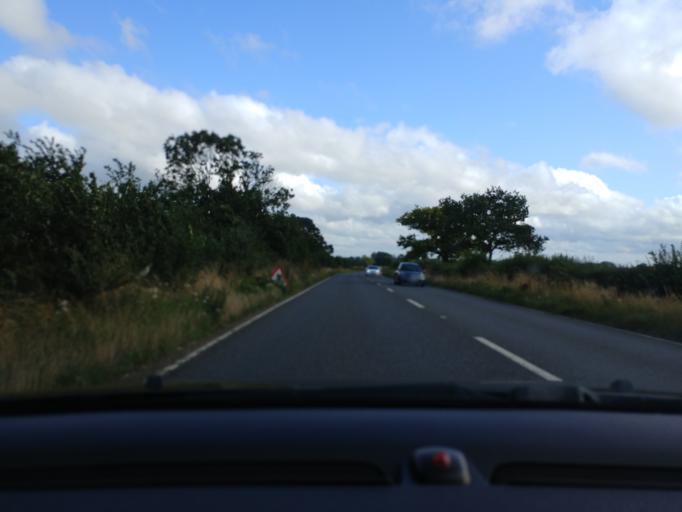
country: GB
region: England
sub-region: Oxfordshire
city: Kidlington
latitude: 51.8749
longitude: -1.2295
